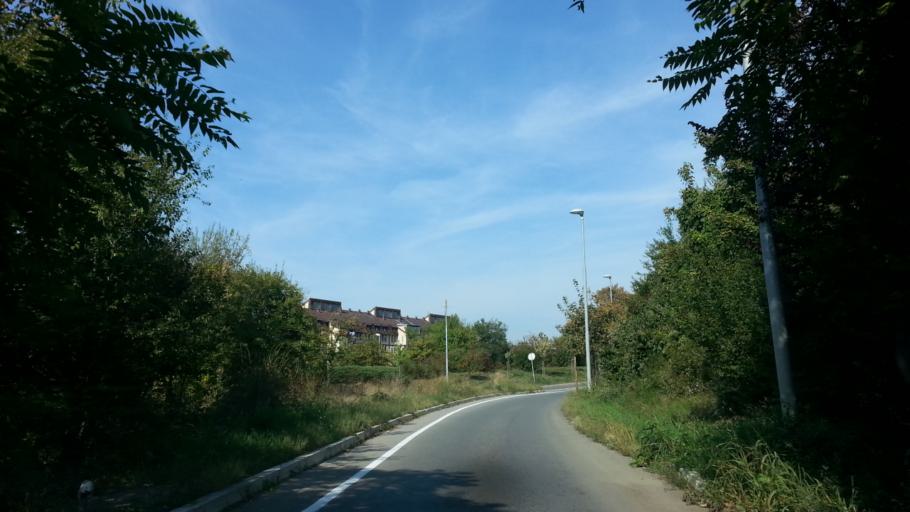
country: RS
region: Central Serbia
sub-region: Belgrade
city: Rakovica
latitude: 44.7413
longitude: 20.4154
